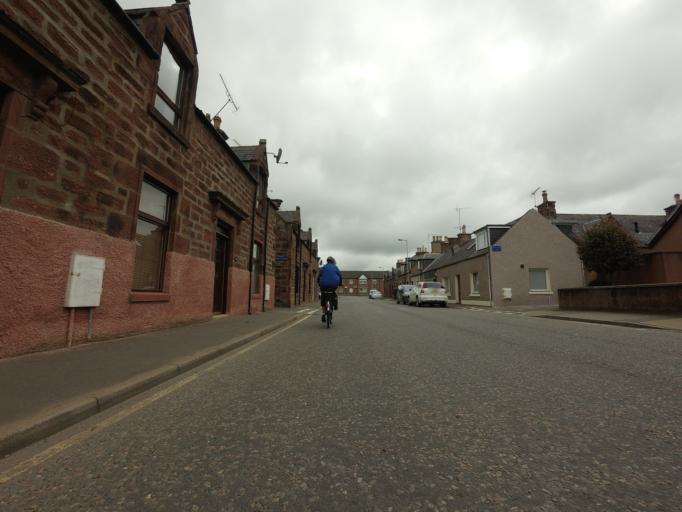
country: GB
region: Scotland
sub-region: Aberdeenshire
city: Turriff
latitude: 57.5376
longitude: -2.4570
